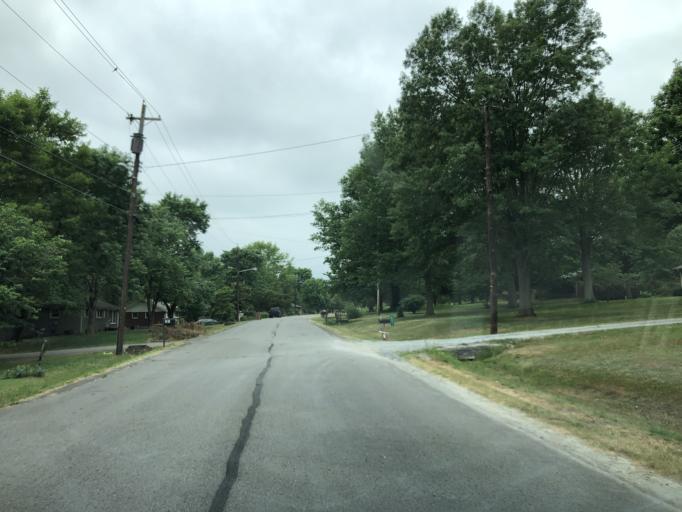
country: US
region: Tennessee
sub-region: Davidson County
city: Goodlettsville
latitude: 36.2797
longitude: -86.7271
